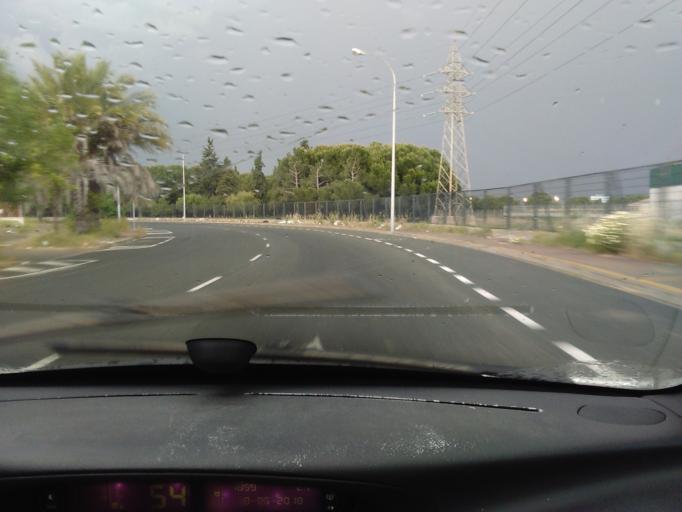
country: ES
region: Andalusia
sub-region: Provincia de Sevilla
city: Sevilla
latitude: 37.3951
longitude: -5.9379
